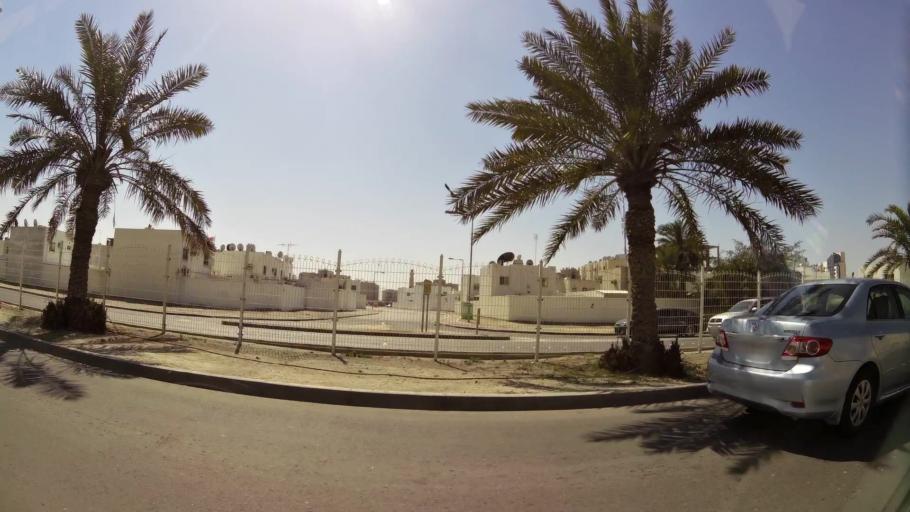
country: BH
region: Manama
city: Manama
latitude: 26.2019
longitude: 50.5893
